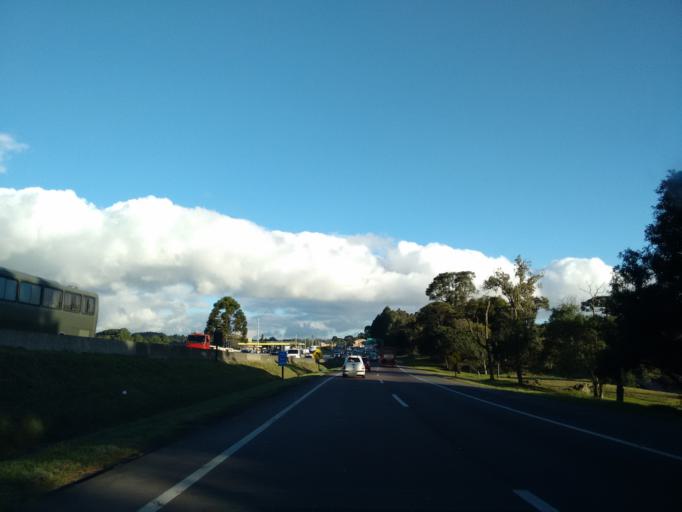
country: BR
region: Parana
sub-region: Sao Jose Dos Pinhais
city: Sao Jose dos Pinhais
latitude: -25.6939
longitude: -49.1448
